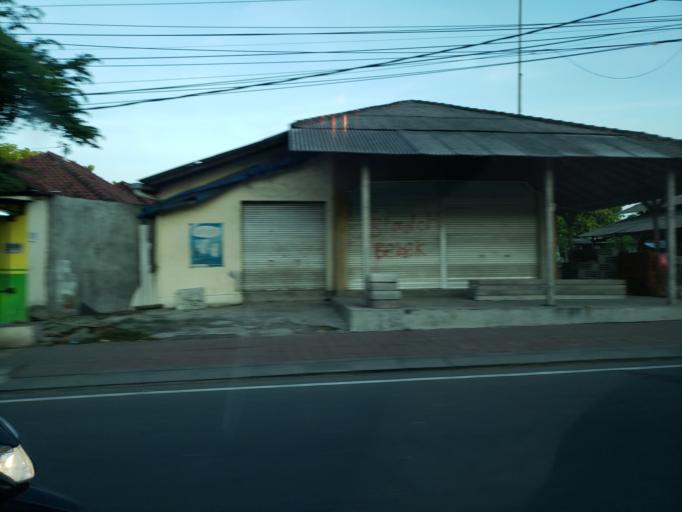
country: ID
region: Bali
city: Jimbaran
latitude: -8.7834
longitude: 115.1787
